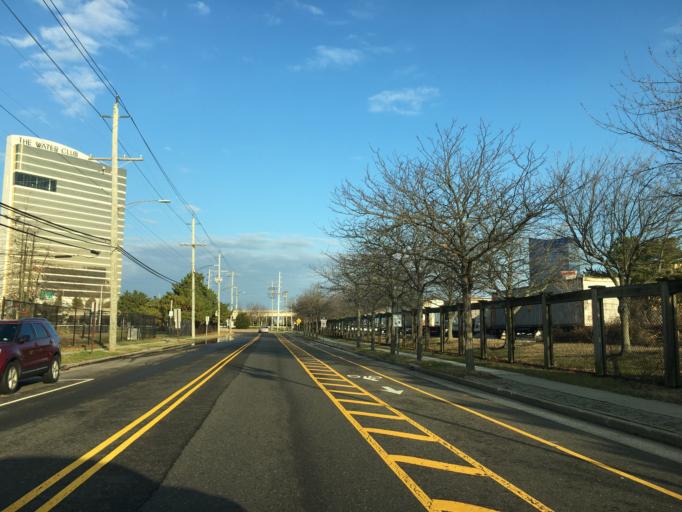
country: US
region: New Jersey
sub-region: Atlantic County
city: Atlantic City
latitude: 39.3757
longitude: -74.4293
